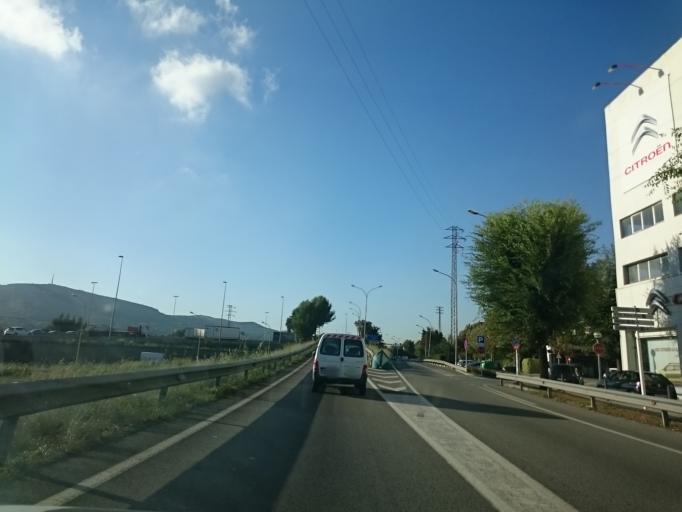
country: ES
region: Catalonia
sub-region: Provincia de Barcelona
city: Molins de Rei
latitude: 41.4104
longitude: 2.0148
